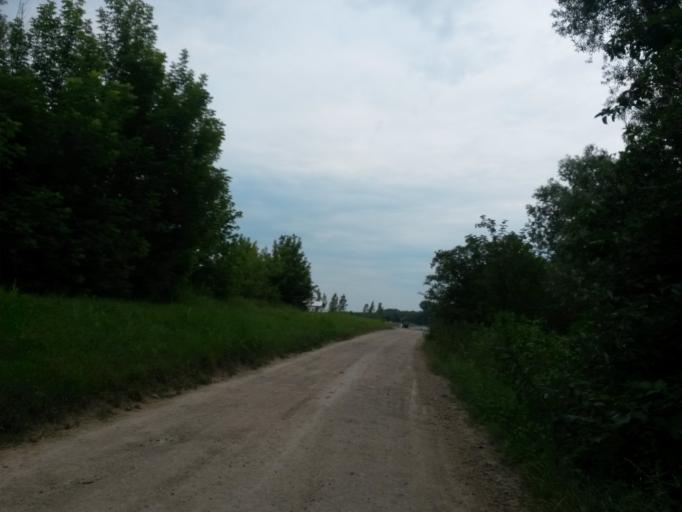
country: HR
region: Osjecko-Baranjska
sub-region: Grad Osijek
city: Bilje
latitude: 45.5917
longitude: 18.7398
